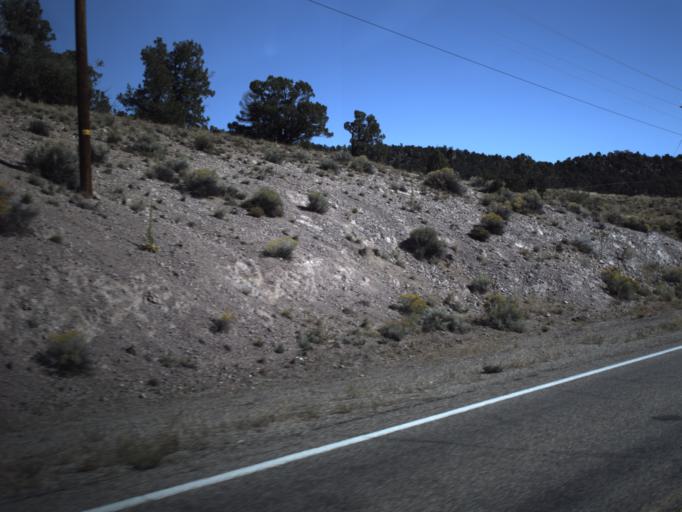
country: US
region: Utah
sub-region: Iron County
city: Cedar City
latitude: 37.6368
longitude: -113.2843
